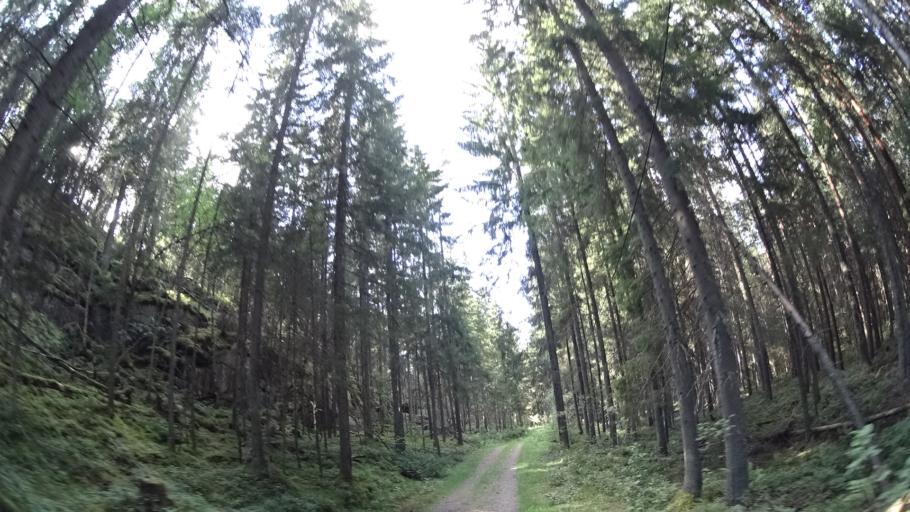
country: FI
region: Uusimaa
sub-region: Helsinki
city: Vihti
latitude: 60.3744
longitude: 24.3775
